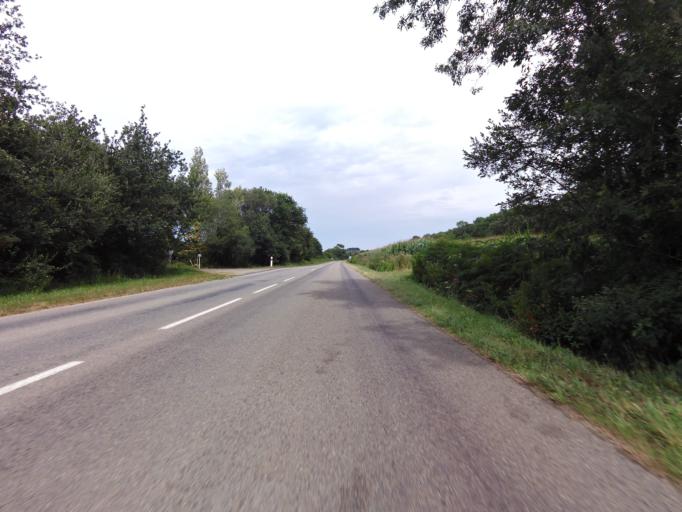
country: FR
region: Brittany
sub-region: Departement du Finistere
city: Poullan-sur-Mer
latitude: 48.0771
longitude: -4.4460
